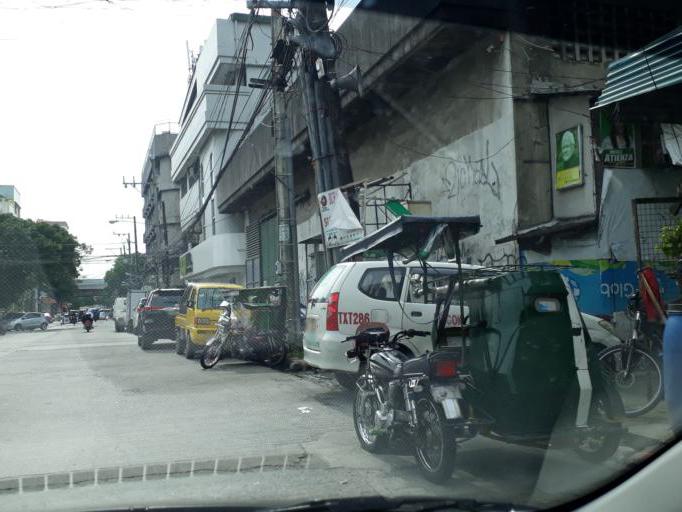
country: PH
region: Metro Manila
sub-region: City of Manila
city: Manila
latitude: 14.6206
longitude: 120.9845
